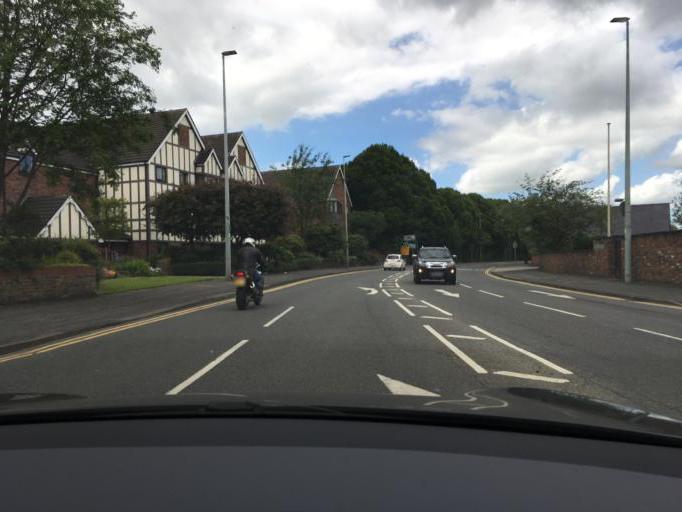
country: GB
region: England
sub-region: Cheshire East
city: Knutsford
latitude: 53.3032
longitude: -2.3750
